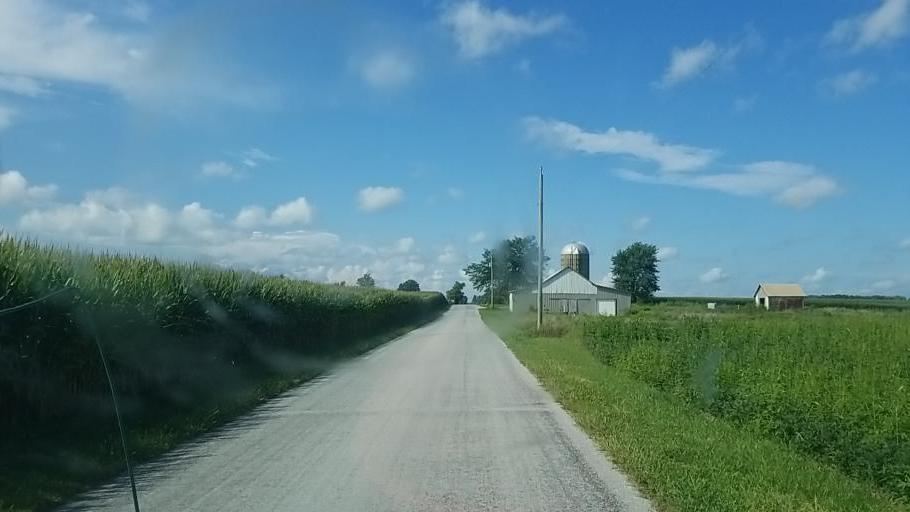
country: US
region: Ohio
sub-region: Hardin County
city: Kenton
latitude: 40.6800
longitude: -83.5310
